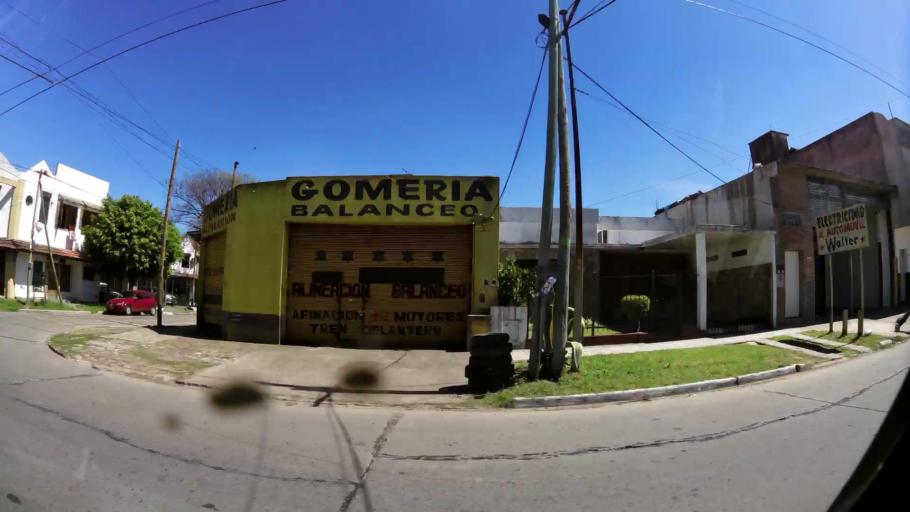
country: AR
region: Buenos Aires
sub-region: Partido de Quilmes
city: Quilmes
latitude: -34.7202
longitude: -58.2822
